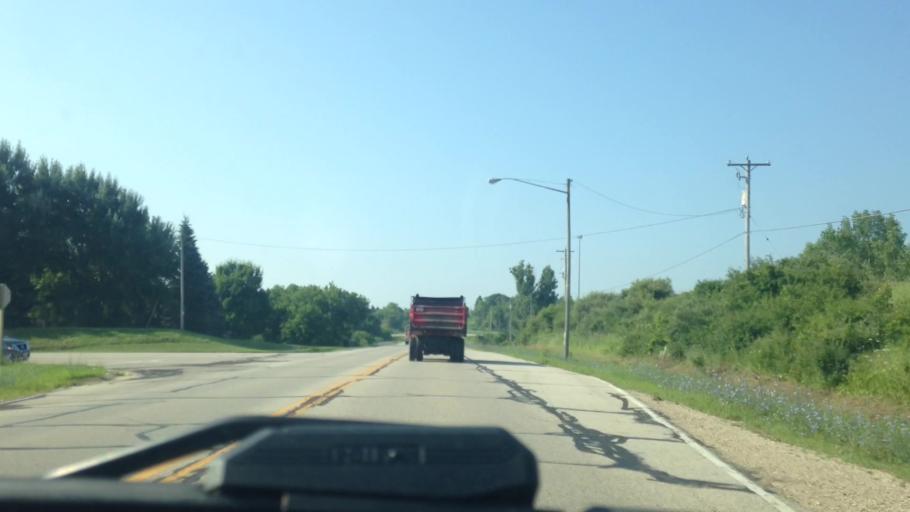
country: US
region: Wisconsin
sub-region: Waukesha County
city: Merton
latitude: 43.1695
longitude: -88.2625
